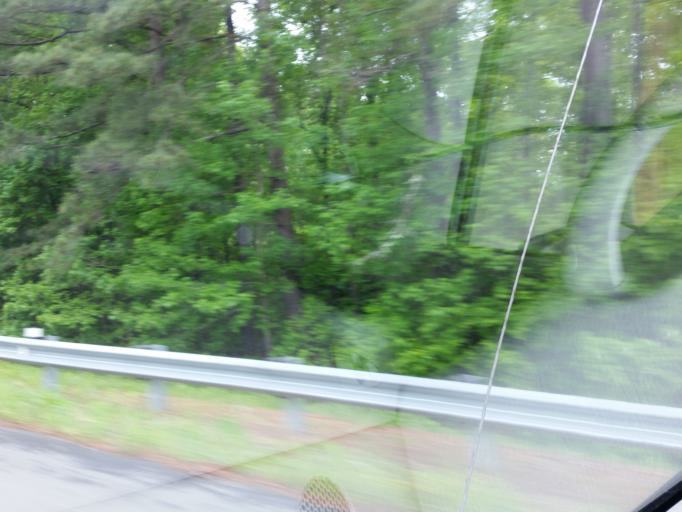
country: US
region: Georgia
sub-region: Spalding County
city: Griffin
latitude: 33.1795
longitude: -84.2696
